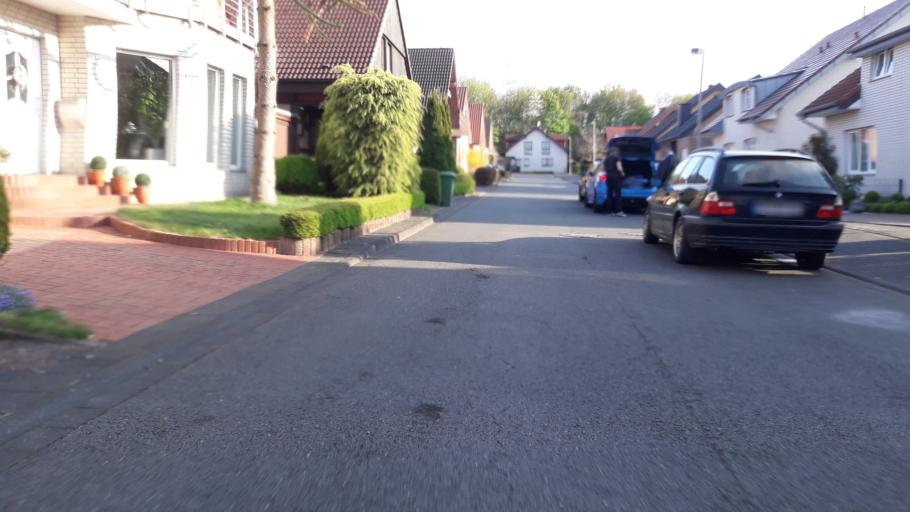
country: DE
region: North Rhine-Westphalia
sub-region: Regierungsbezirk Detmold
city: Paderborn
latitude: 51.7099
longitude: 8.7995
